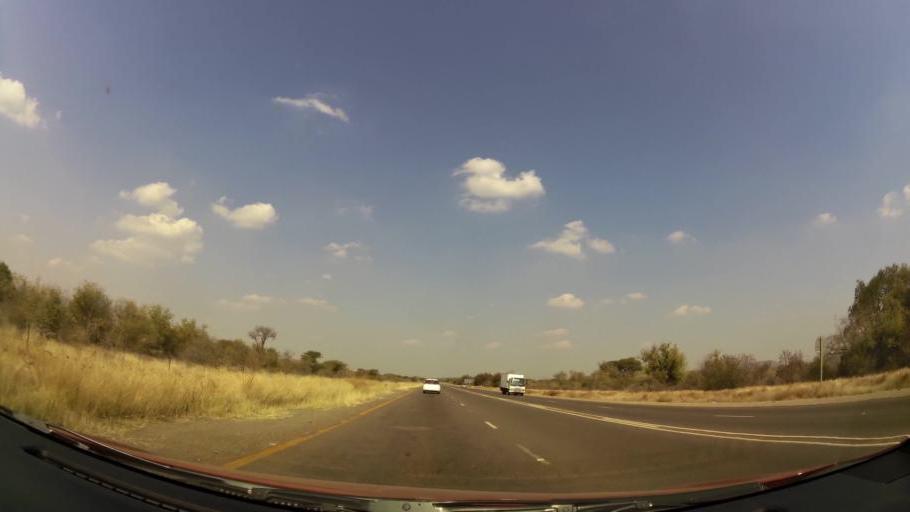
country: ZA
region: North-West
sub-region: Bojanala Platinum District Municipality
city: Mogwase
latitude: -25.4227
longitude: 27.0799
